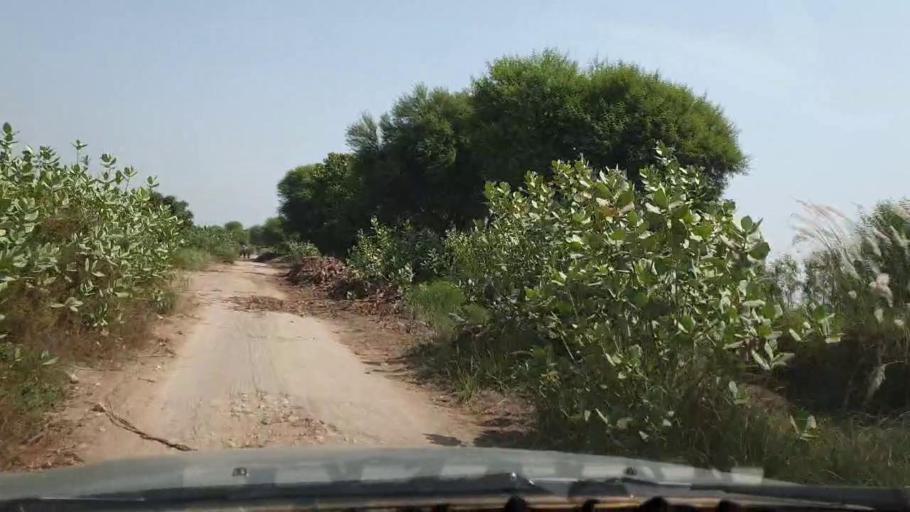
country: PK
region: Sindh
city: Matli
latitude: 25.1754
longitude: 68.6594
